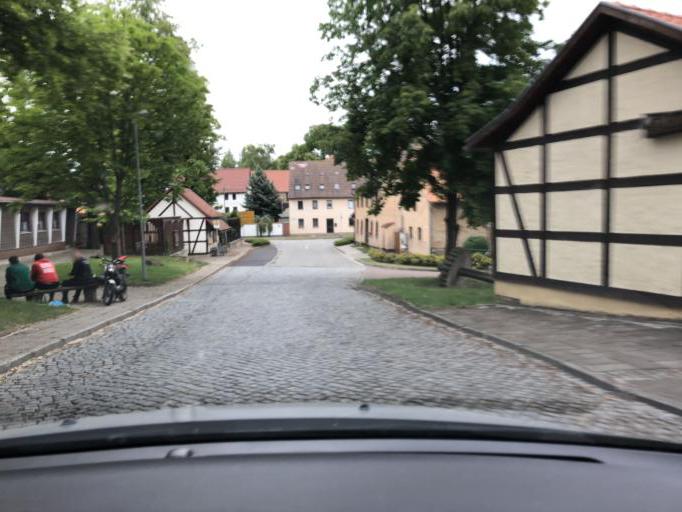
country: DE
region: Thuringia
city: Willerstedt
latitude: 51.0895
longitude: 11.4529
